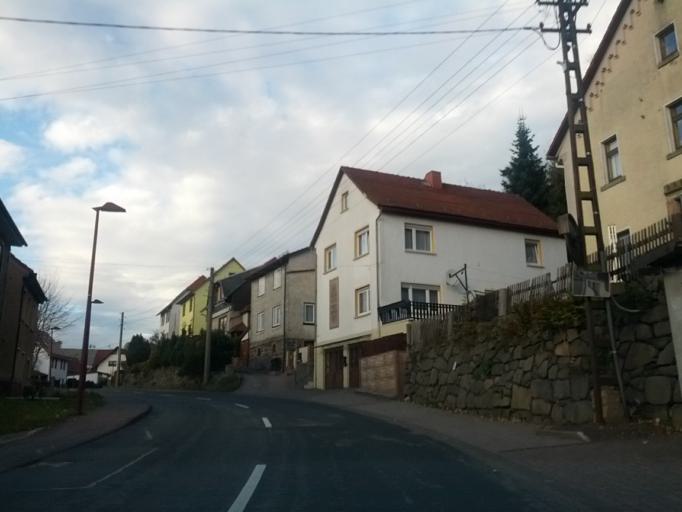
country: DE
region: Thuringia
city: Brotterode
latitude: 50.8267
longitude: 10.4453
